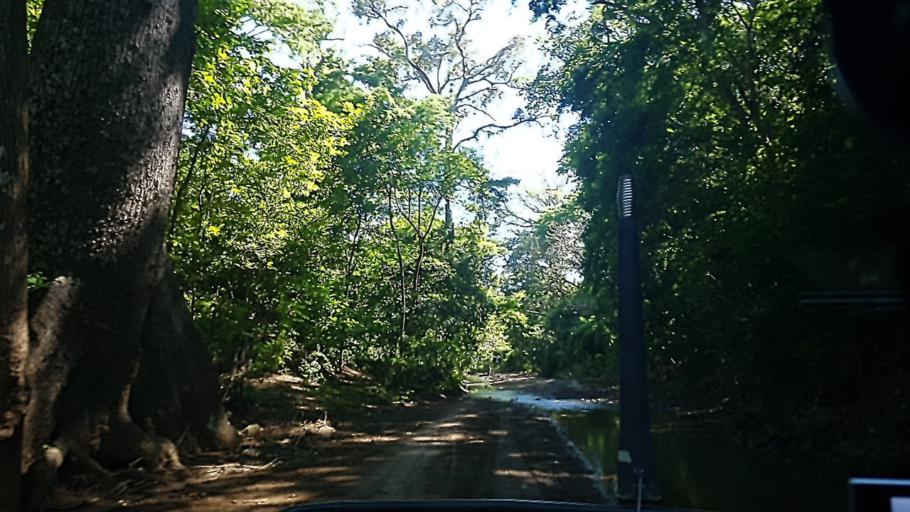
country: NI
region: Rivas
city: Tola
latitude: 11.5566
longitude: -86.0892
